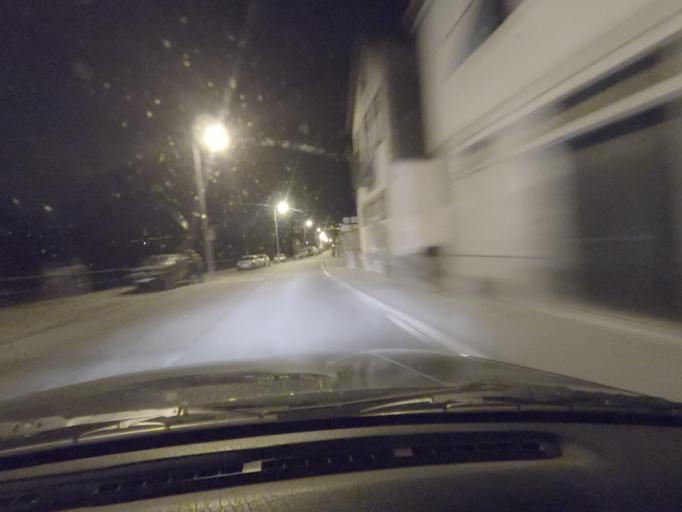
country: PT
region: Vila Real
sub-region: Peso da Regua
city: Godim
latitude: 41.1720
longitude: -7.7963
